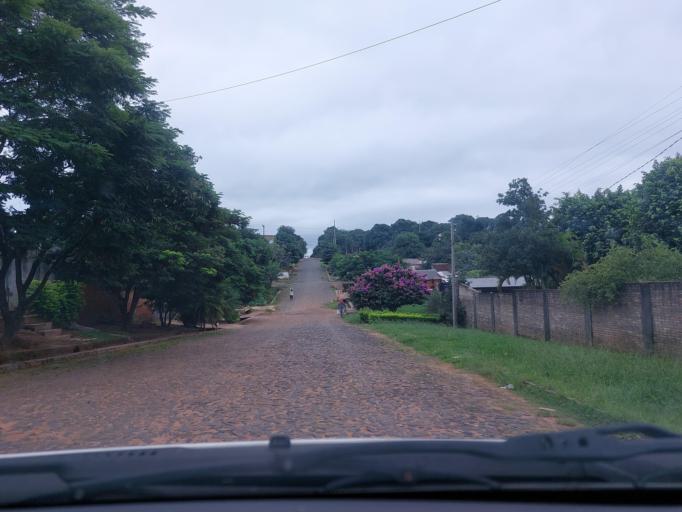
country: PY
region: San Pedro
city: Guayaybi
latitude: -24.6679
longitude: -56.4382
